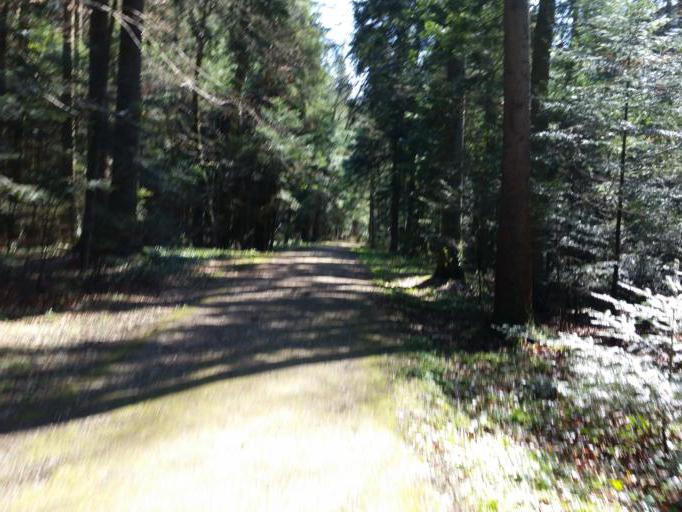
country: CH
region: Thurgau
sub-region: Arbon District
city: Amriswil
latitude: 47.5476
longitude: 9.3229
